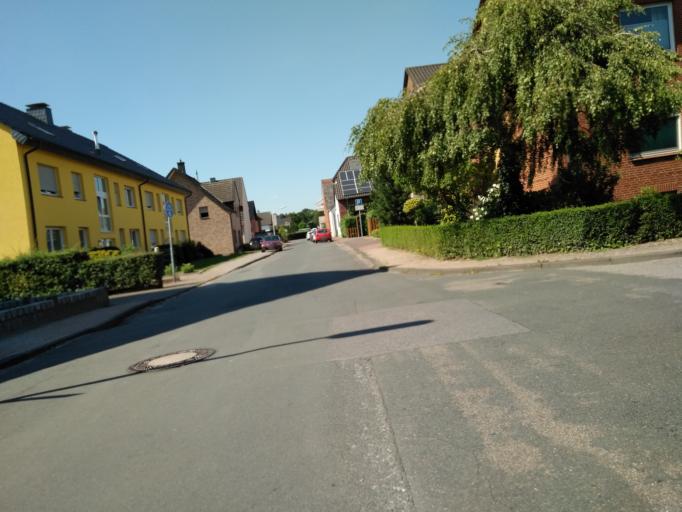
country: DE
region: North Rhine-Westphalia
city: Dorsten
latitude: 51.6789
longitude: 6.9465
